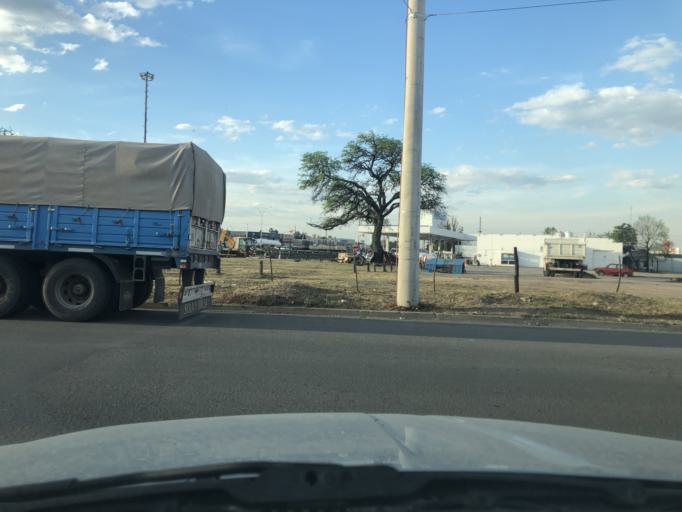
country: AR
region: Cordoba
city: Jesus Maria
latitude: -30.9789
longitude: -64.0847
